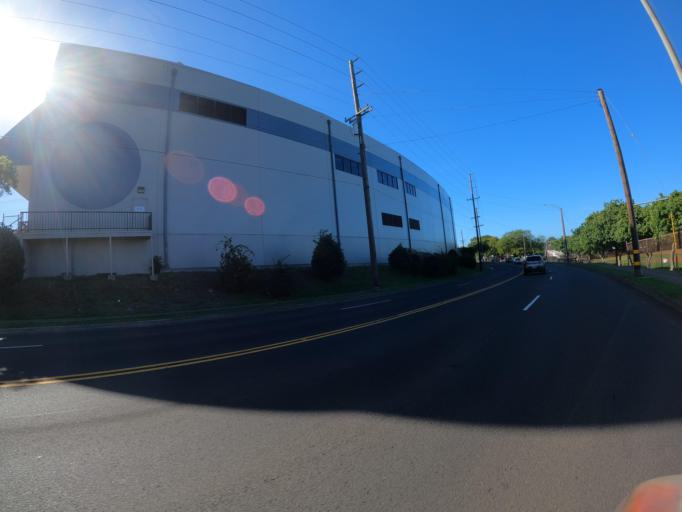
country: US
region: Hawaii
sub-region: Honolulu County
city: Halawa
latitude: 21.3579
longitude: -157.9285
